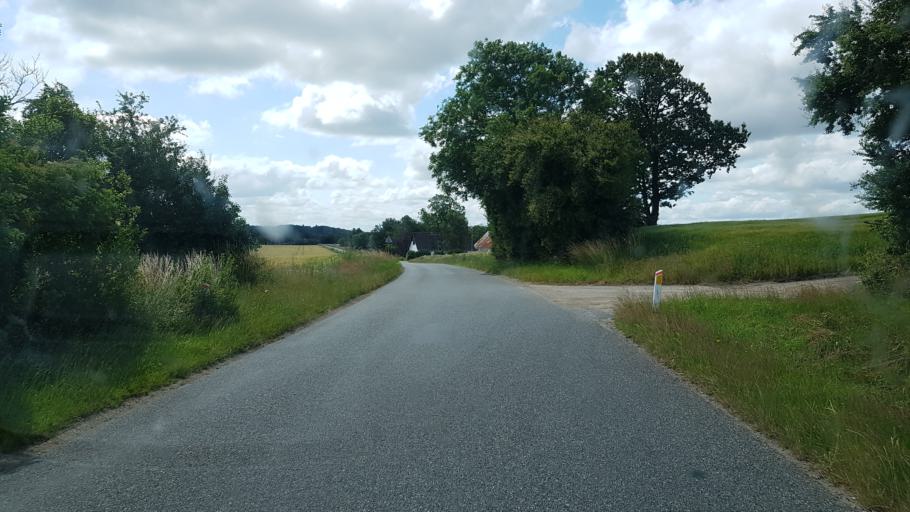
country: DK
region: South Denmark
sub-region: Vejen Kommune
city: Brorup
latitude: 55.4497
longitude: 8.9977
